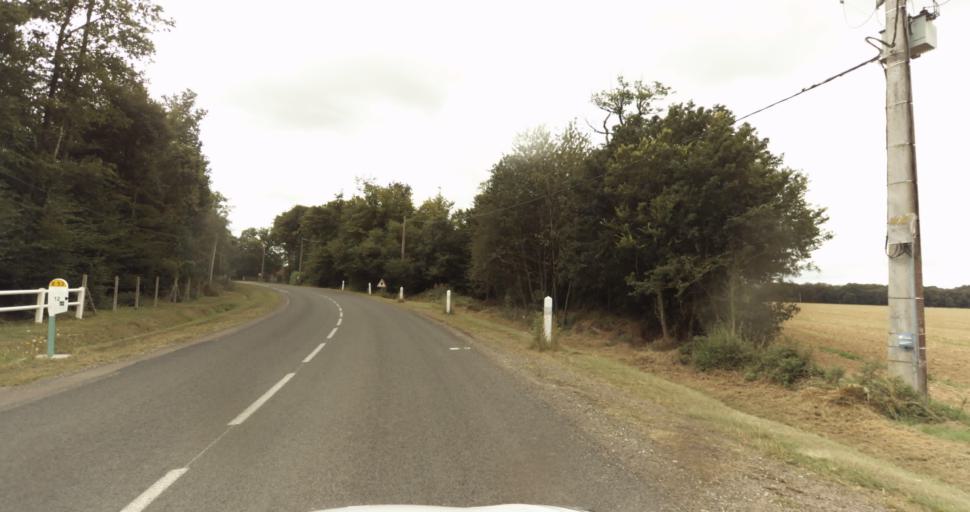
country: FR
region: Haute-Normandie
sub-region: Departement de l'Eure
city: La Madeleine-de-Nonancourt
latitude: 48.8143
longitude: 1.2160
